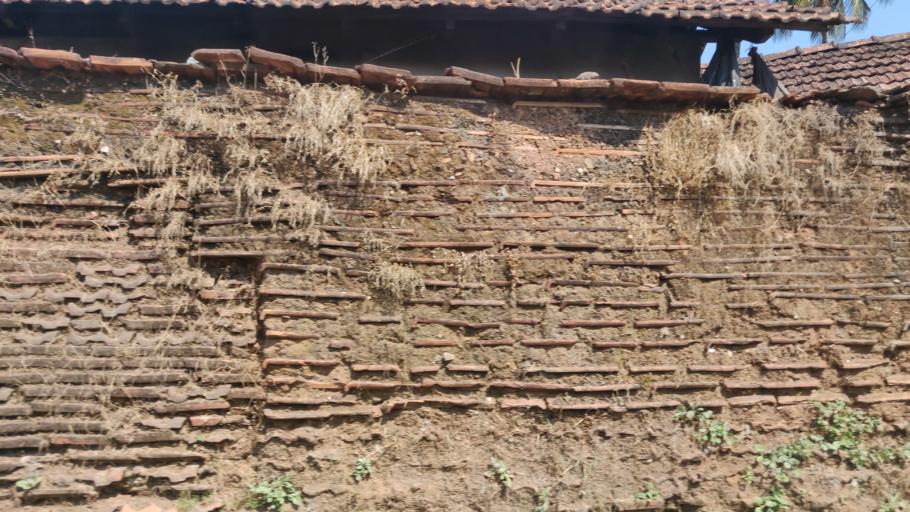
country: IN
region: Karnataka
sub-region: Dakshina Kannada
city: Ullal
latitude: 12.8471
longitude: 74.8418
